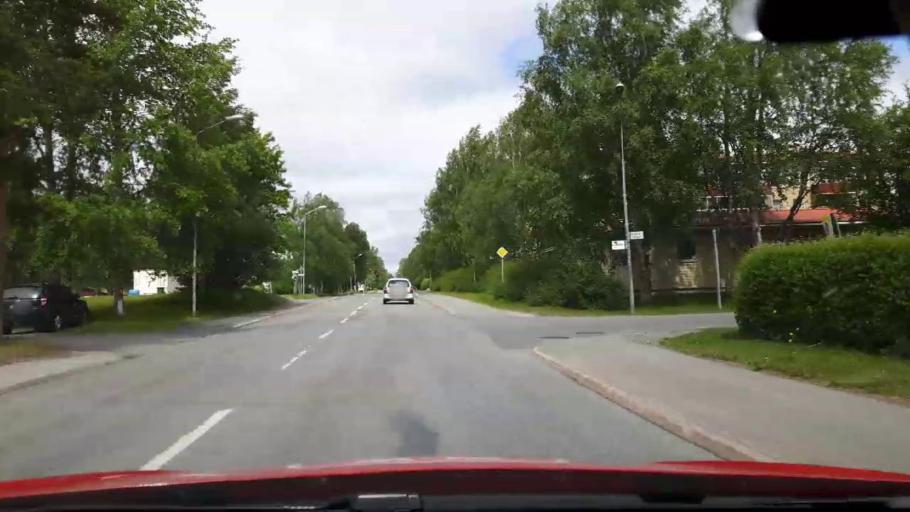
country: SE
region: Jaemtland
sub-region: Krokoms Kommun
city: Krokom
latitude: 63.3284
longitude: 14.4478
